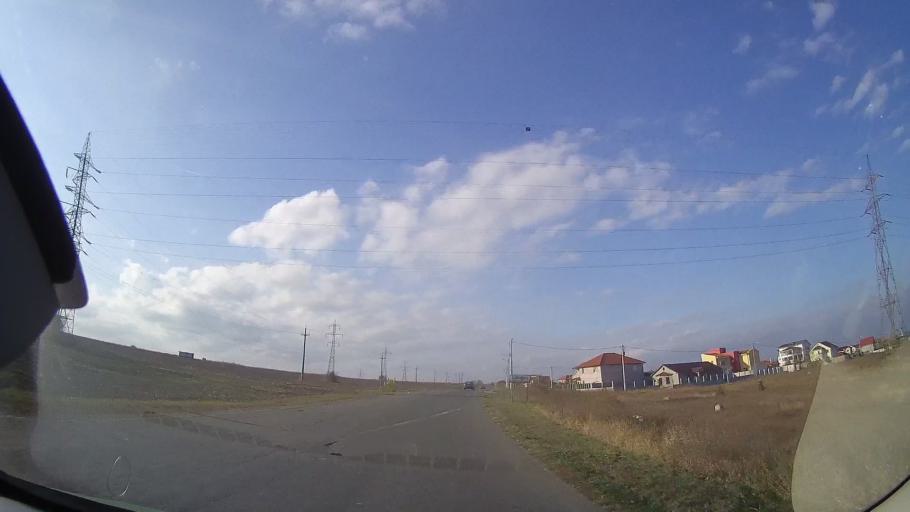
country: RO
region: Constanta
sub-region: Comuna Limanu
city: Limanu
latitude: 43.7908
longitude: 28.5493
